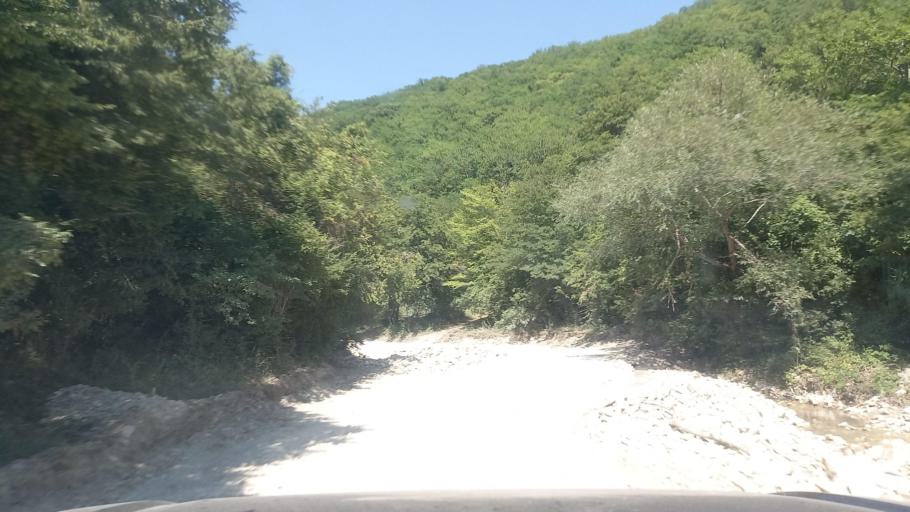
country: RU
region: Krasnodarskiy
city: Lermontovo
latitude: 44.3292
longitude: 38.8017
